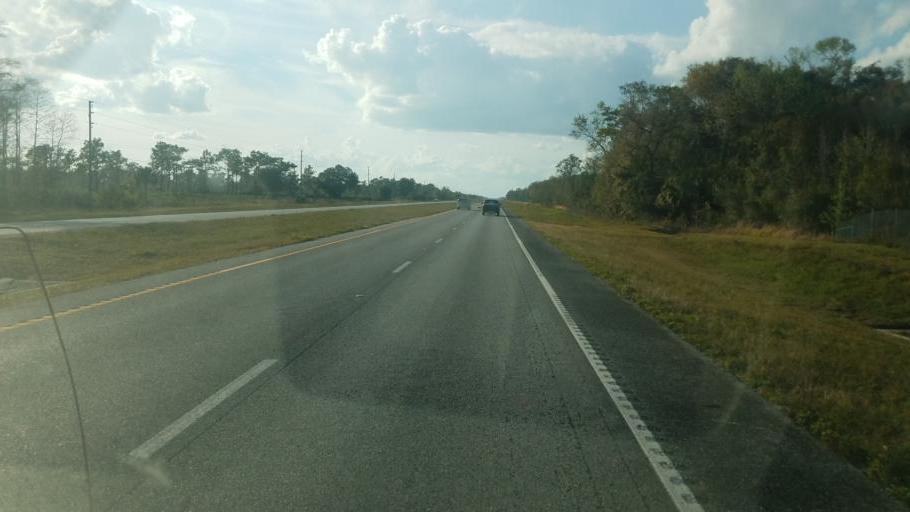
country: US
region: Florida
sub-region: Osceola County
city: Saint Cloud
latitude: 28.1332
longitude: -81.0182
